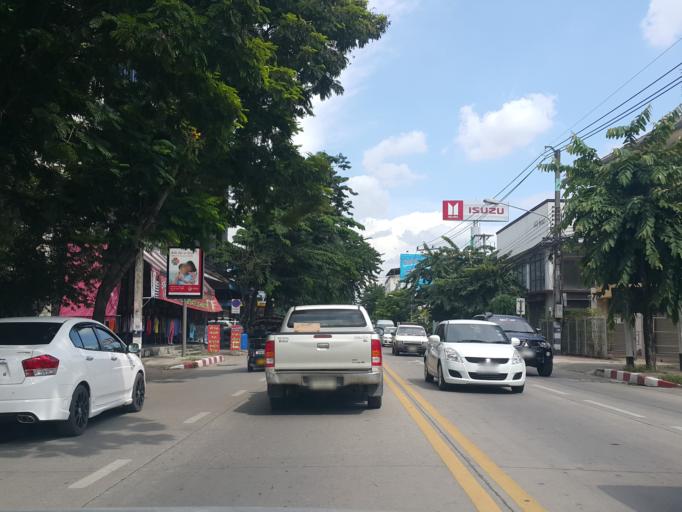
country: TH
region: Chiang Mai
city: Chiang Mai
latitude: 18.7851
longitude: 99.0186
